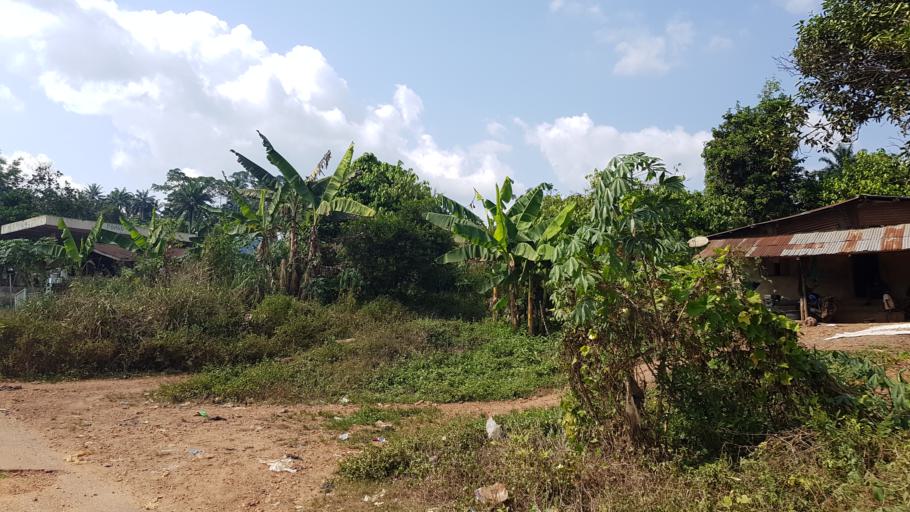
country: NG
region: Osun
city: Ifetedo
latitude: 7.0171
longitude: 4.6358
